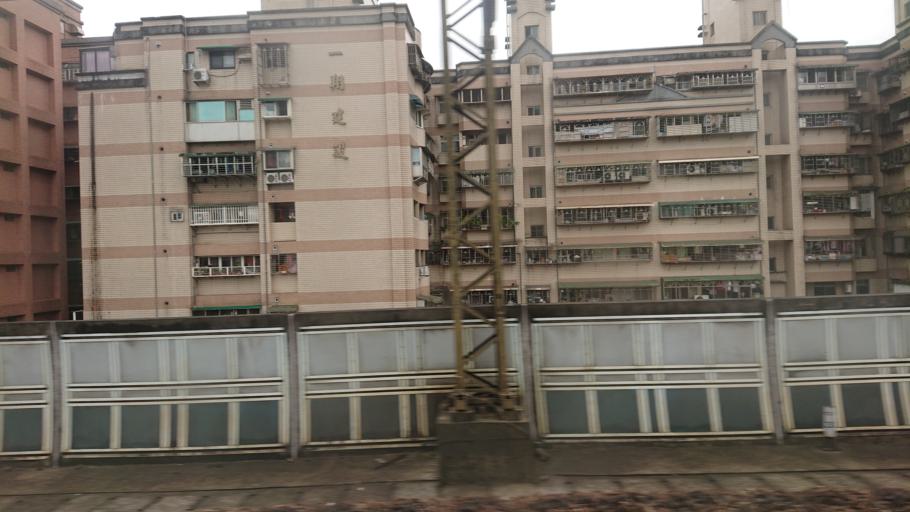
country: TW
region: Taiwan
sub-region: Keelung
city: Keelung
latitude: 25.0735
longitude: 121.6655
